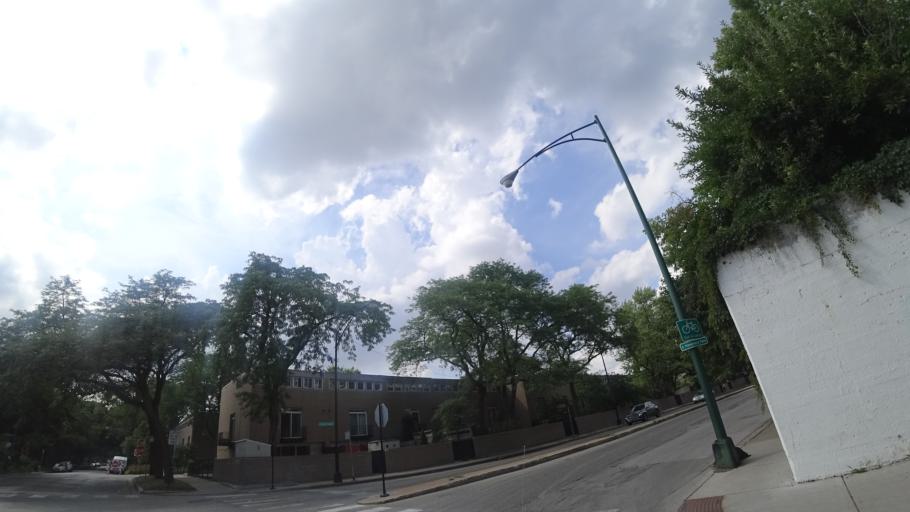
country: US
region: Illinois
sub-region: Cook County
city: Chicago
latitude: 41.7934
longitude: -87.5877
